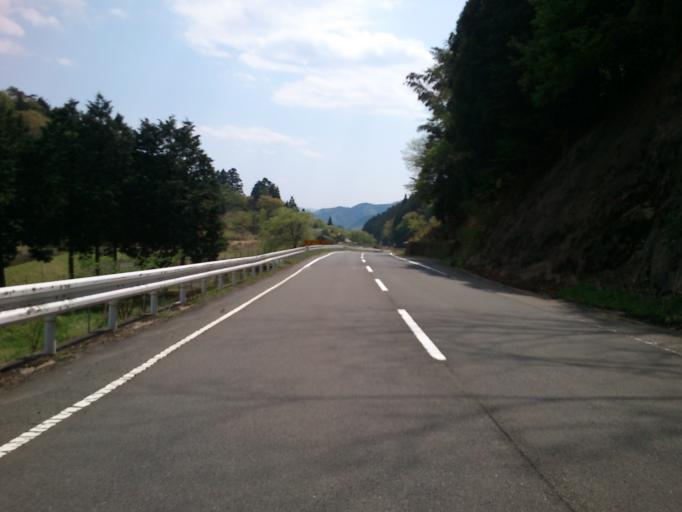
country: JP
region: Hyogo
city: Toyooka
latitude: 35.4030
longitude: 134.9485
